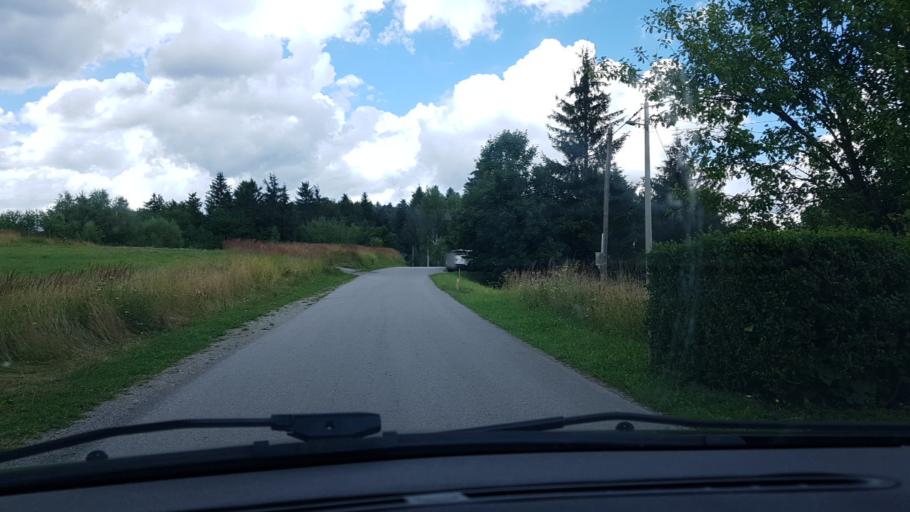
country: HR
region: Primorsko-Goranska
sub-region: Grad Delnice
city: Delnice
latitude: 45.3680
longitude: 14.7106
